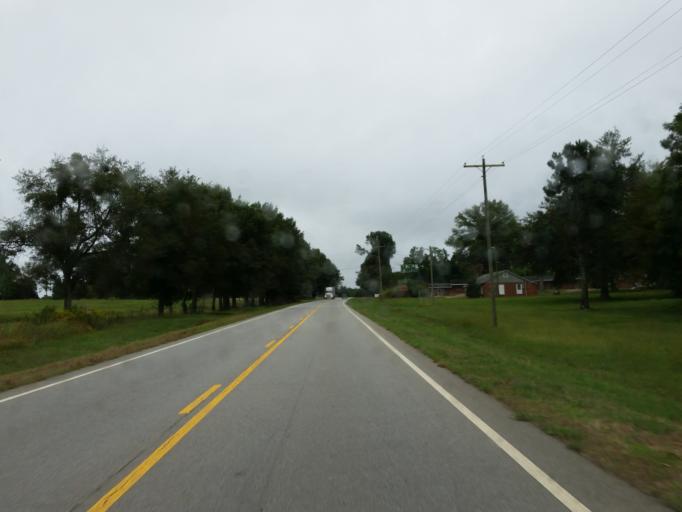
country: US
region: Georgia
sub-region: Lamar County
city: Barnesville
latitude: 32.9710
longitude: -84.1131
